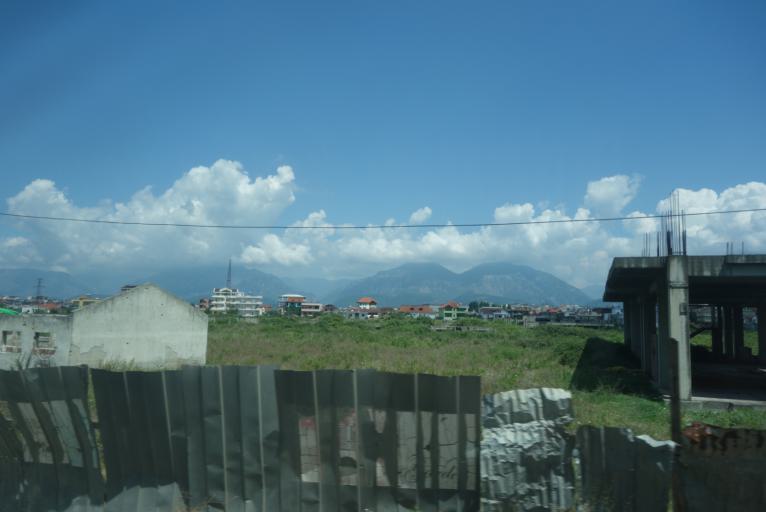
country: AL
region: Tirane
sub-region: Rrethi i Tiranes
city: Paskuqan
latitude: 41.3451
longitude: 19.7756
